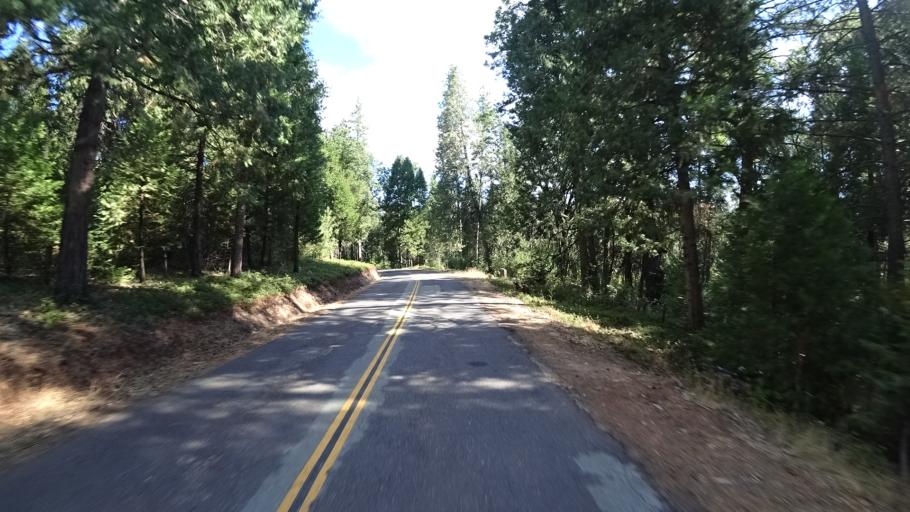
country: US
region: California
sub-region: Amador County
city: Pioneer
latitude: 38.3858
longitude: -120.4518
